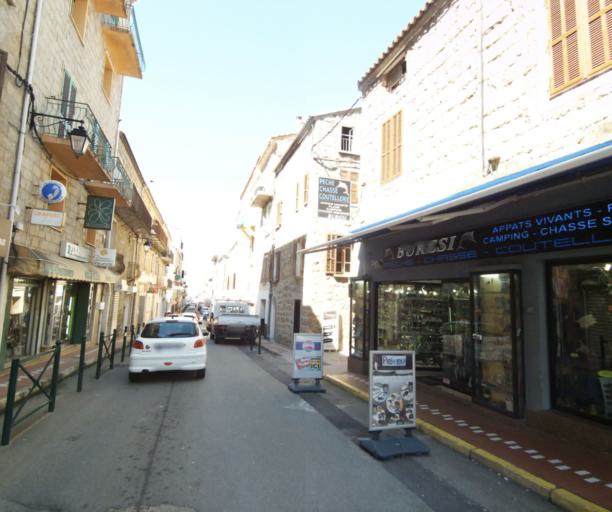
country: FR
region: Corsica
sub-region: Departement de la Corse-du-Sud
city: Propriano
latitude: 41.6762
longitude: 8.9061
